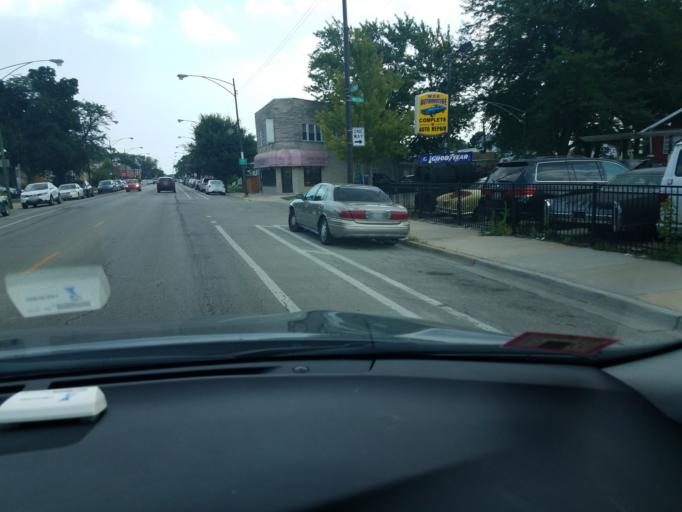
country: US
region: Illinois
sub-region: Cook County
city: Harwood Heights
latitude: 41.9894
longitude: -87.7769
